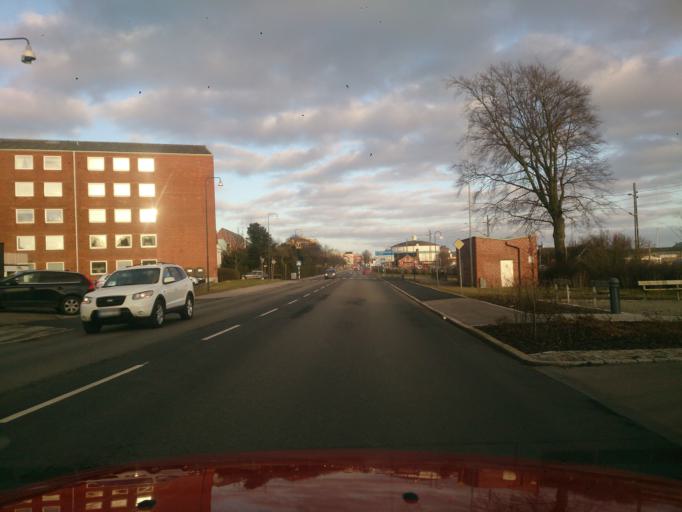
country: SE
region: Skane
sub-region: Ystads Kommun
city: Ystad
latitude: 55.4272
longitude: 13.8127
